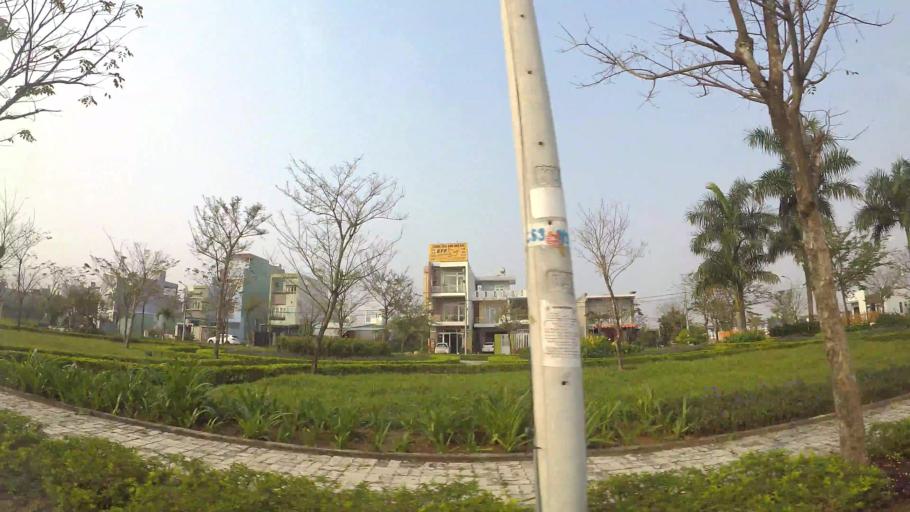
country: VN
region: Da Nang
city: Cam Le
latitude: 16.0147
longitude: 108.2181
